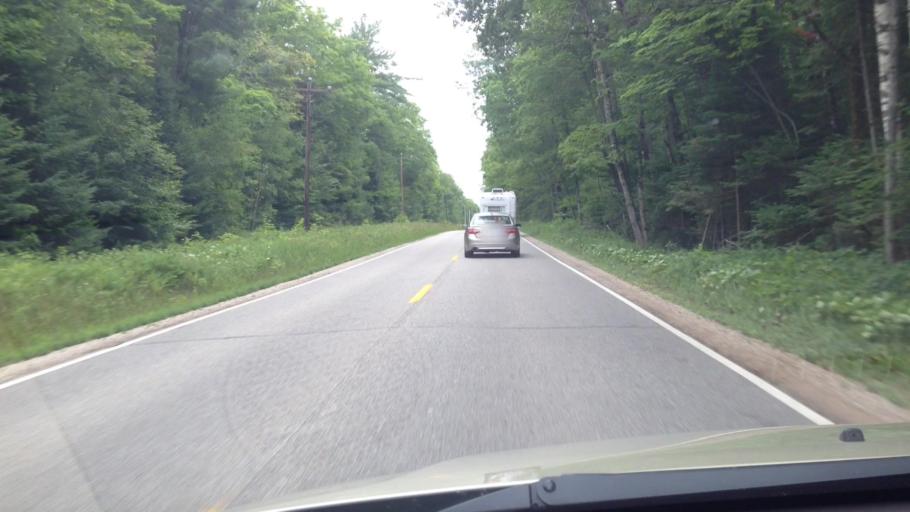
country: US
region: Michigan
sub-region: Mackinac County
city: Saint Ignace
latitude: 46.0568
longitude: -85.1460
